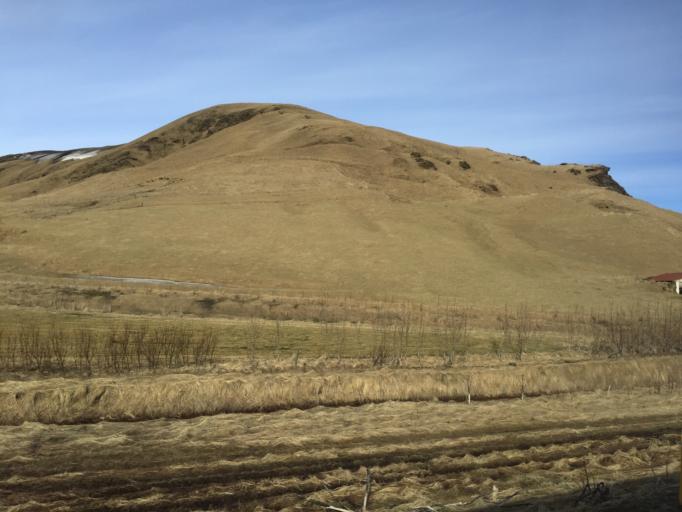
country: IS
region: South
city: Vestmannaeyjar
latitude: 63.4474
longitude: -19.1229
